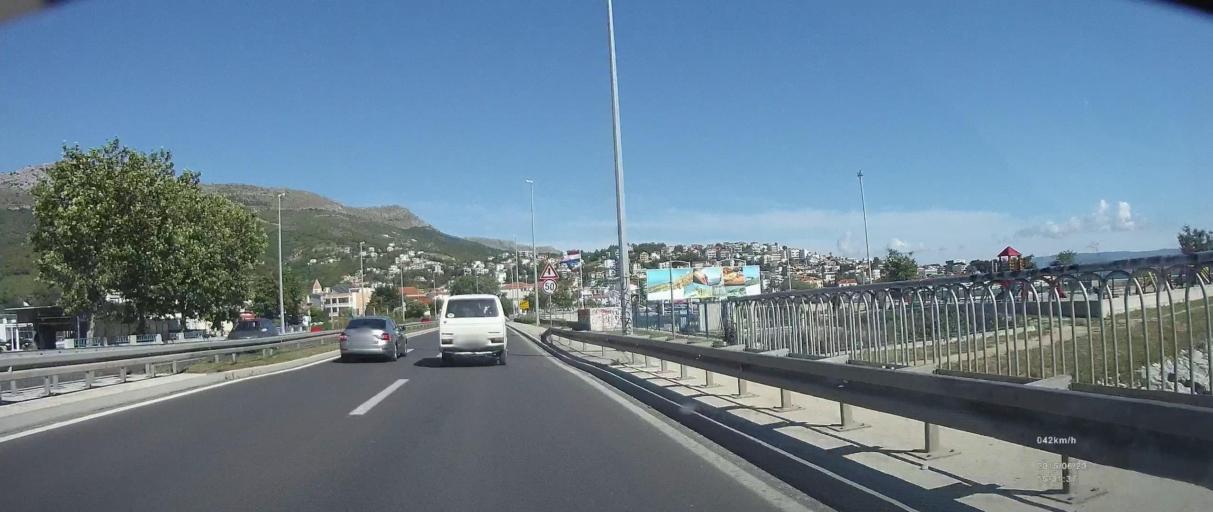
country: HR
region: Splitsko-Dalmatinska
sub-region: Grad Split
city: Stobrec
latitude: 43.5048
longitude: 16.5310
